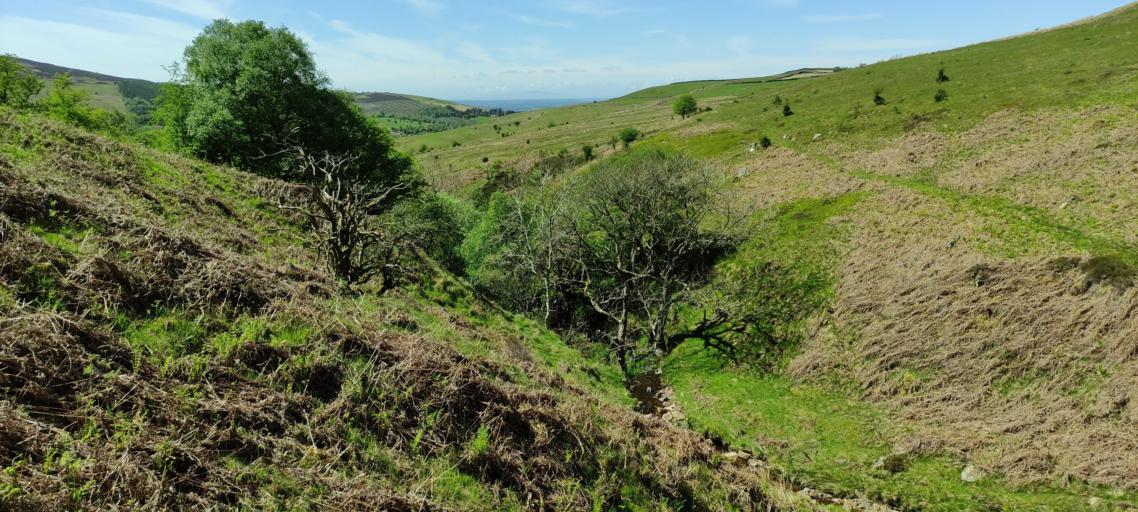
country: GB
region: England
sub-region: Cumbria
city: Brampton
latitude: 54.8900
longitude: -2.6574
